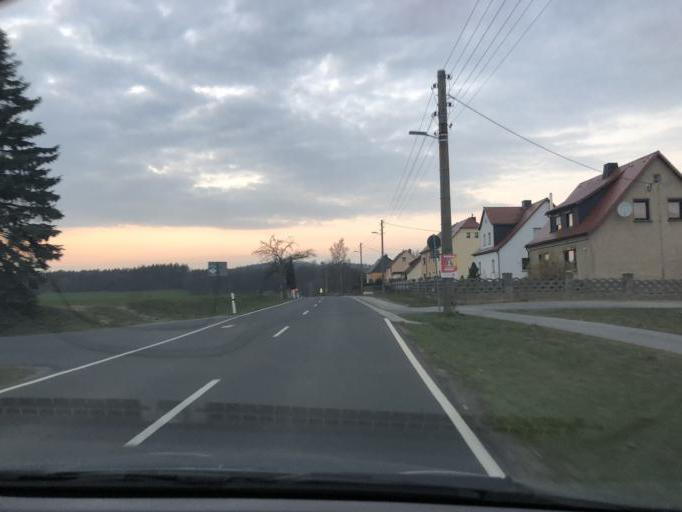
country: DE
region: Saxony
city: Neukirch
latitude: 51.2588
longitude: 13.9502
